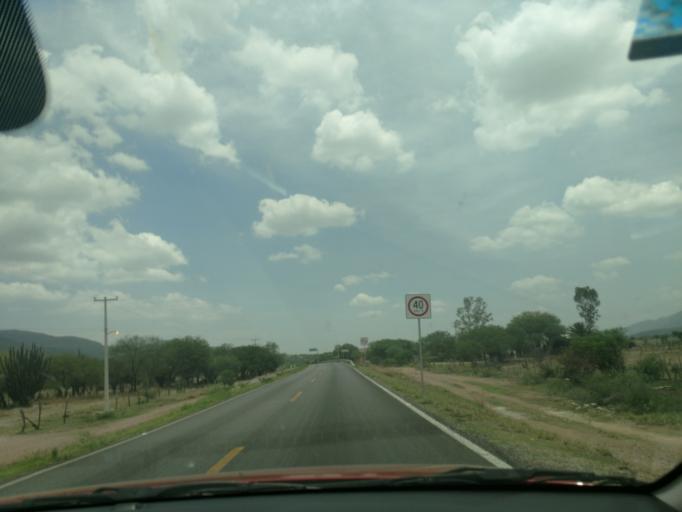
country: MX
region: San Luis Potosi
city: Villa Juarez
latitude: 22.0186
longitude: -100.3889
